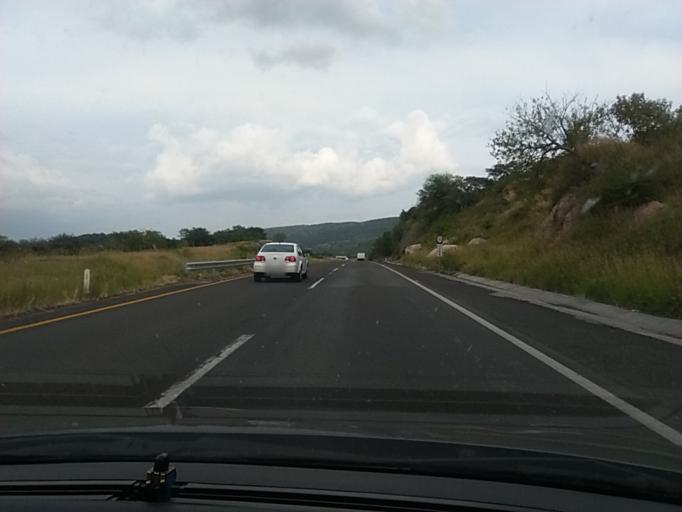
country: MX
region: Mexico
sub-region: Chapultepec
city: Chucandiro
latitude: 19.8876
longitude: -101.3232
